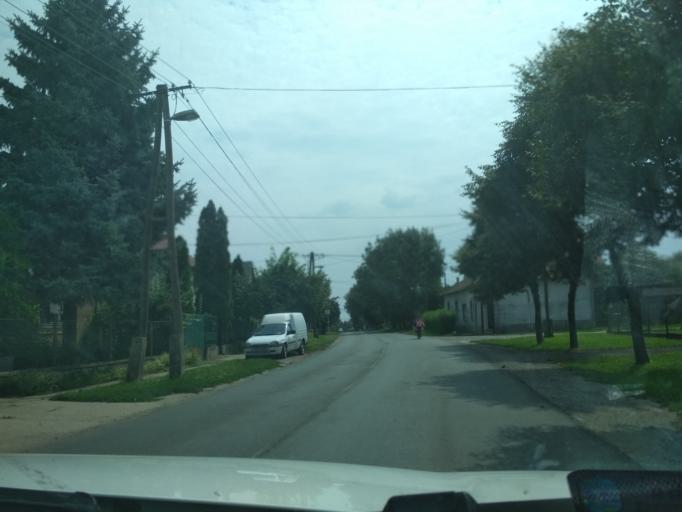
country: HU
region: Jasz-Nagykun-Szolnok
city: Tiszafured
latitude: 47.6141
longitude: 20.7694
